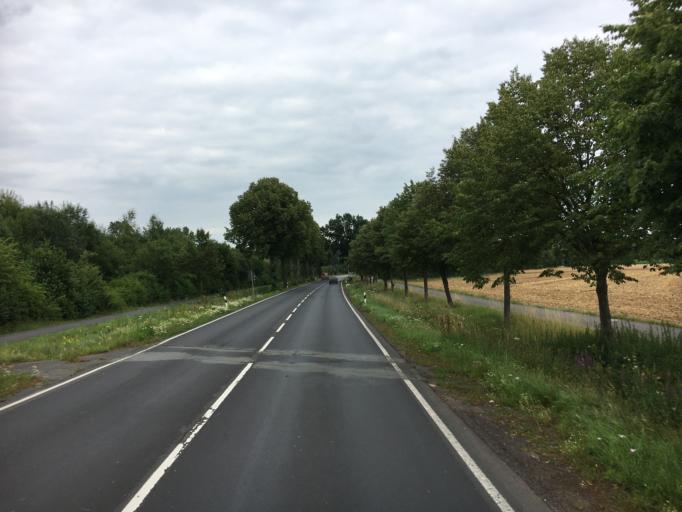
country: DE
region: Hesse
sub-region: Regierungsbezirk Giessen
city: Colbe
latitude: 50.8618
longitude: 8.8081
